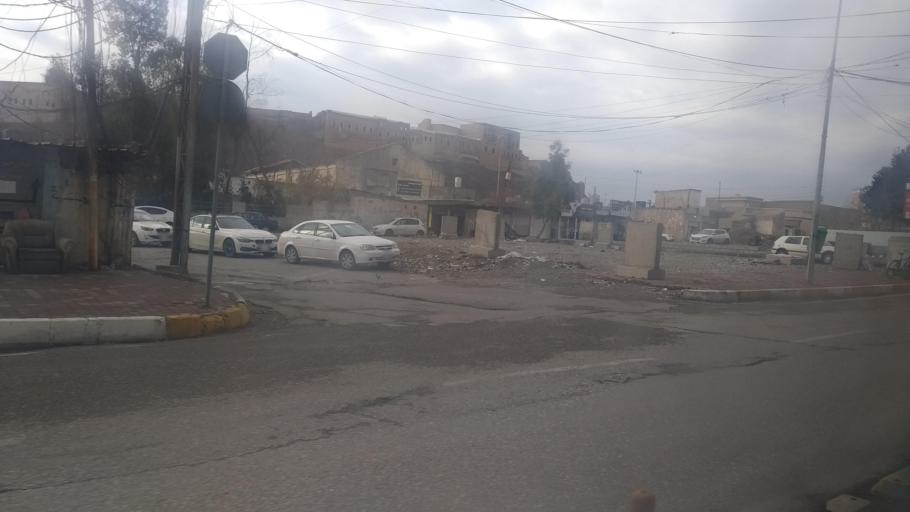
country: IQ
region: Arbil
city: Erbil
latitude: 36.1945
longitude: 44.0112
